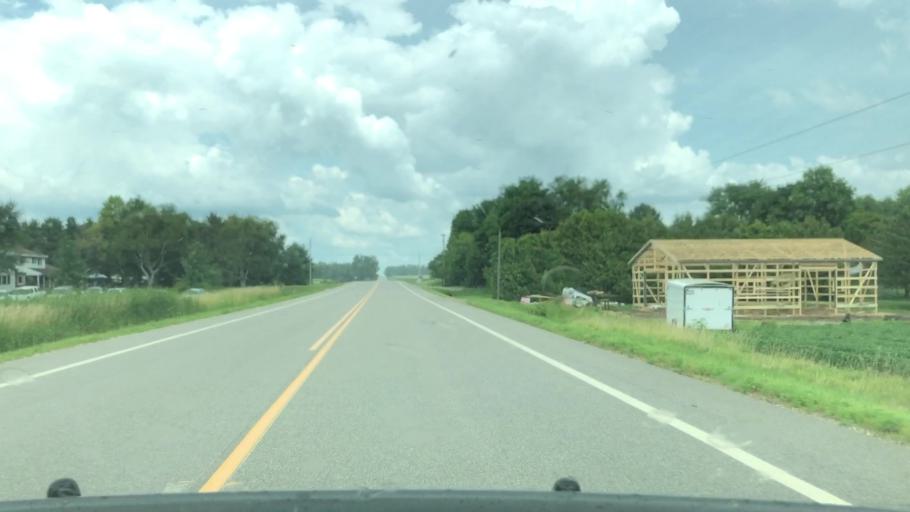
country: US
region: Minnesota
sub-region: Olmsted County
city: Stewartville
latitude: 43.8732
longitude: -92.5286
